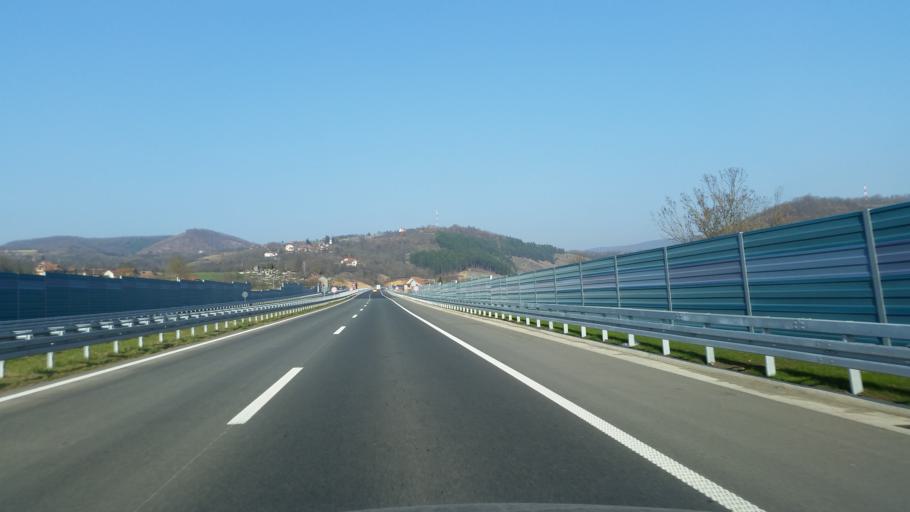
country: RS
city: Prislonica
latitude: 43.9644
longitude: 20.3964
